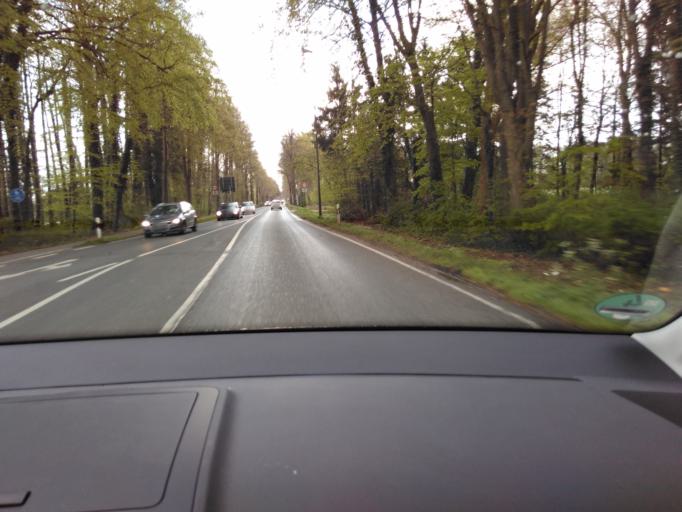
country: DE
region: North Rhine-Westphalia
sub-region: Regierungsbezirk Detmold
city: Guetersloh
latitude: 51.9442
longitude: 8.4290
